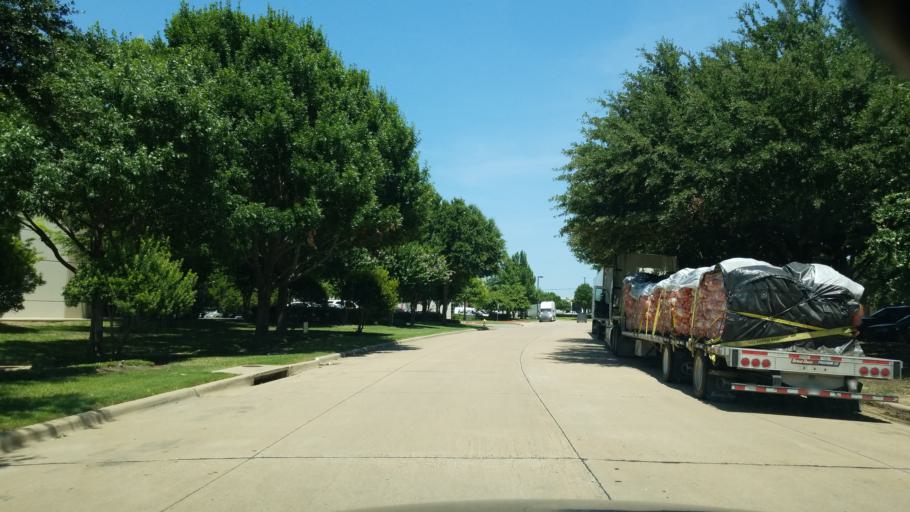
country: US
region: Texas
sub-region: Dallas County
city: Farmers Branch
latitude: 32.9408
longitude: -96.9234
